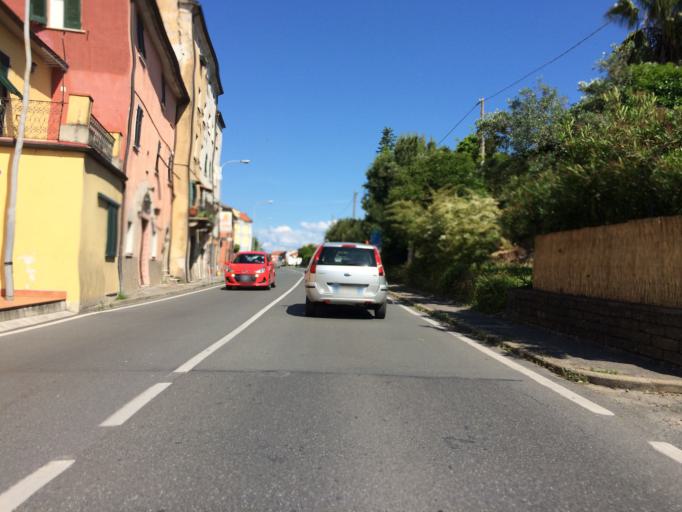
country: IT
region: Tuscany
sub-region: Provincia di Massa-Carrara
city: Borghetto-Melara
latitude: 44.0931
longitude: 9.9928
